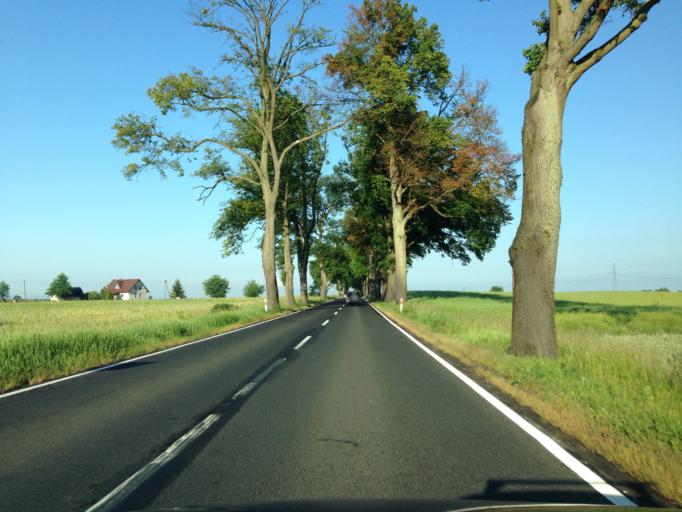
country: PL
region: Kujawsko-Pomorskie
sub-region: Powiat grudziadzki
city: Rogozno
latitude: 53.5787
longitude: 18.8877
